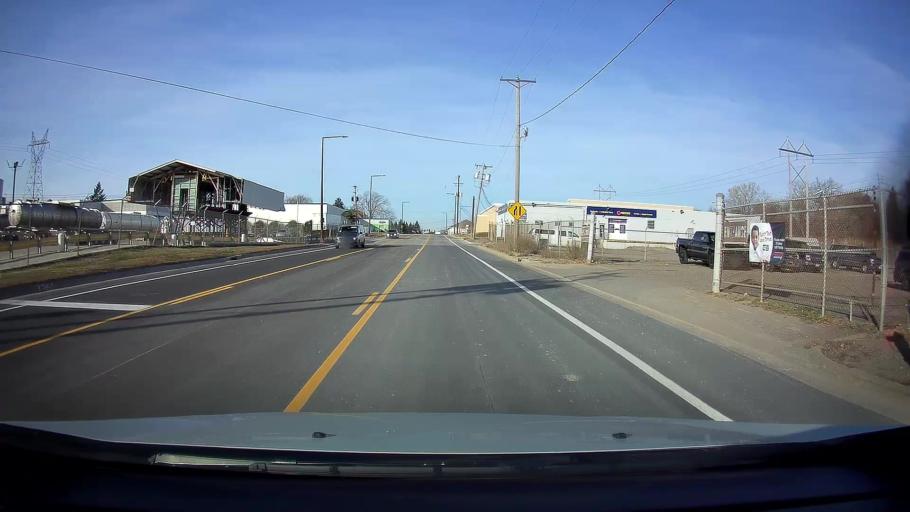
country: US
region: Minnesota
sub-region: Ramsey County
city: Lauderdale
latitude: 44.9739
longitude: -93.1904
